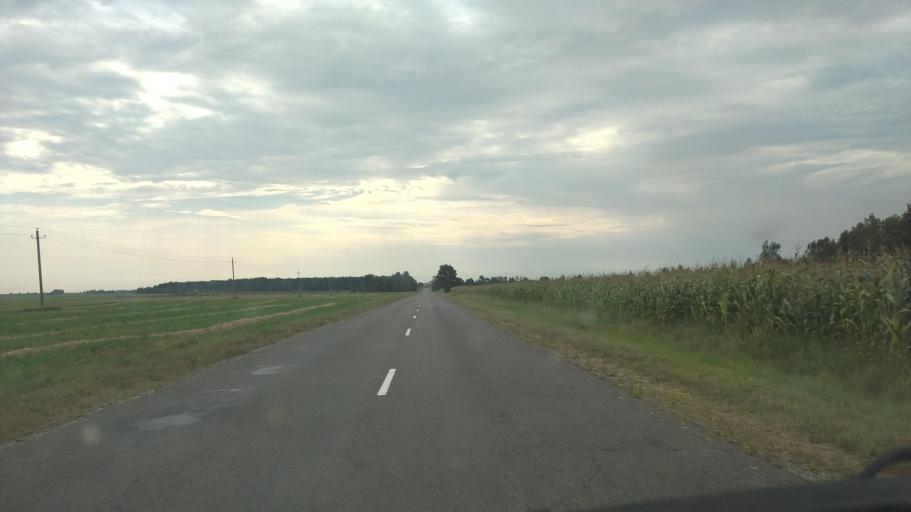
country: BY
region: Brest
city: Byaroza
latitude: 52.5655
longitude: 24.9007
